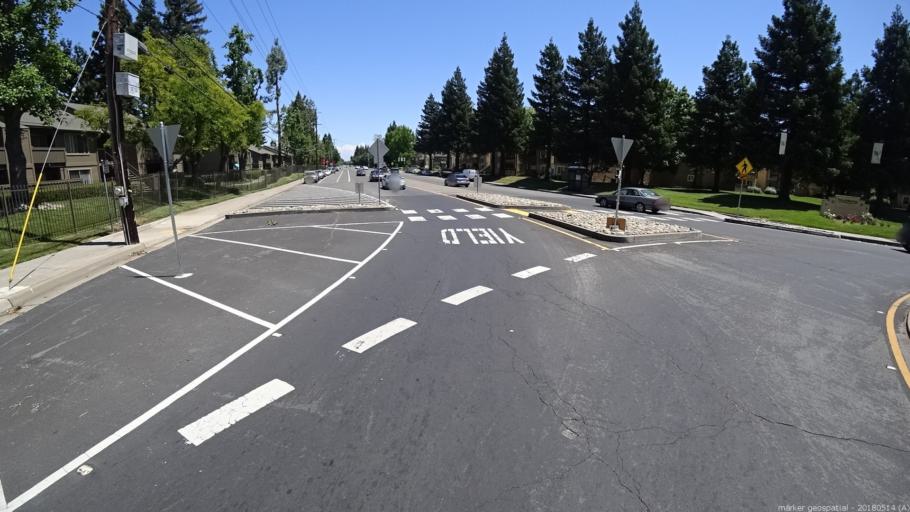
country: US
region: California
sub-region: Sacramento County
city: Sacramento
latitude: 38.6276
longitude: -121.5084
